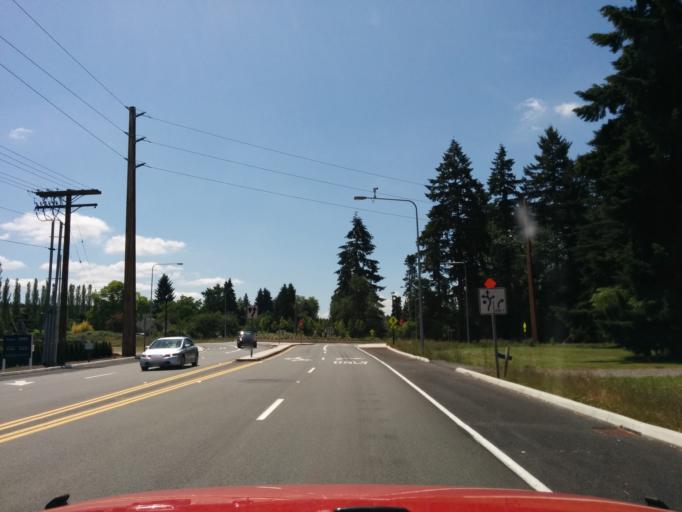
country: US
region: Washington
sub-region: King County
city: Sammamish
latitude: 47.6759
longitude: -122.0791
